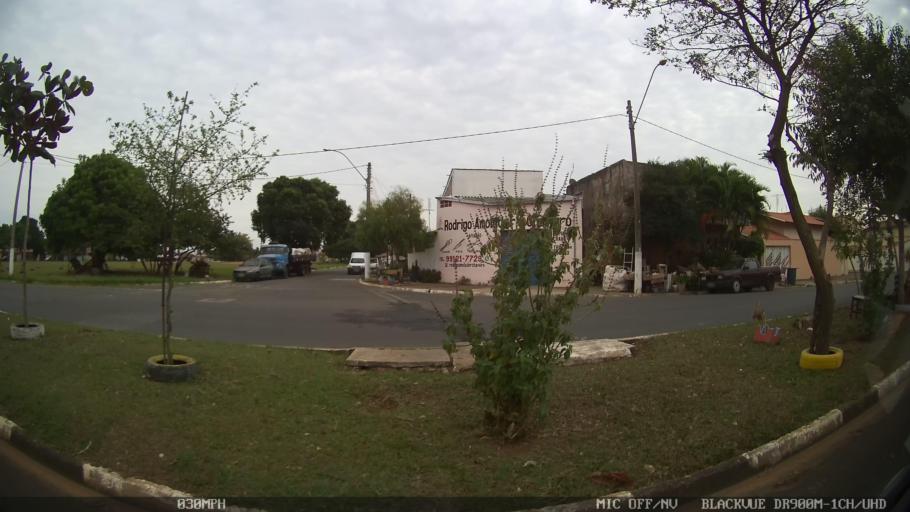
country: BR
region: Sao Paulo
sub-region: Paulinia
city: Paulinia
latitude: -22.7232
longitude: -47.1707
